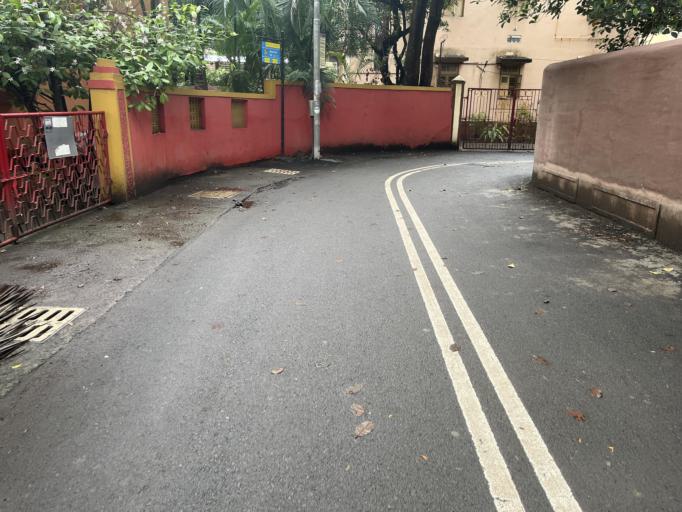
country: IN
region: Maharashtra
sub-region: Mumbai Suburban
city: Borivli
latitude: 19.2338
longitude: 72.8663
